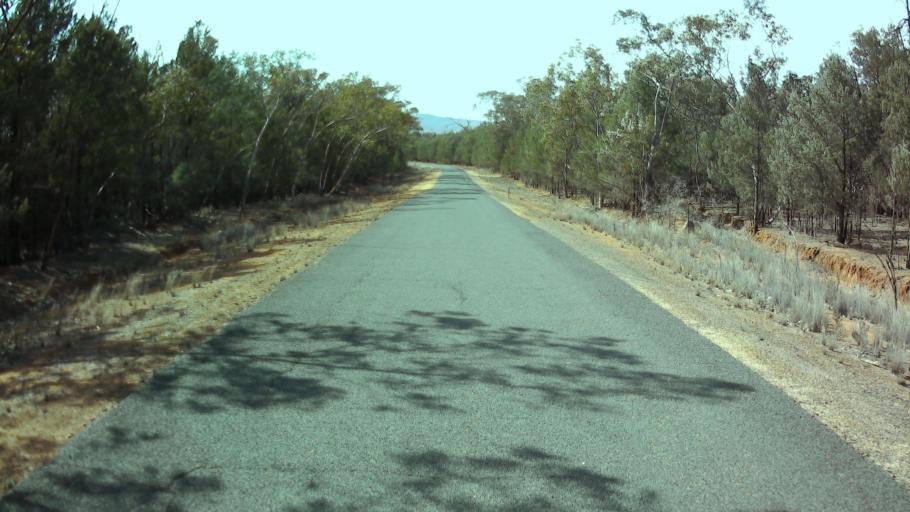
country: AU
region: New South Wales
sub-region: Weddin
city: Grenfell
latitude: -33.7460
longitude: 148.0551
